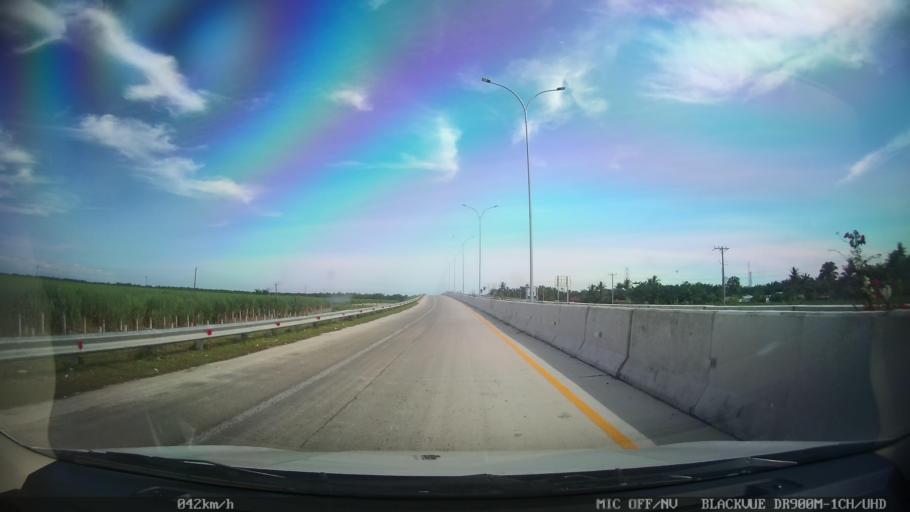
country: ID
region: North Sumatra
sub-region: Kabupaten Langkat
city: Stabat
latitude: 3.7207
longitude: 98.4935
